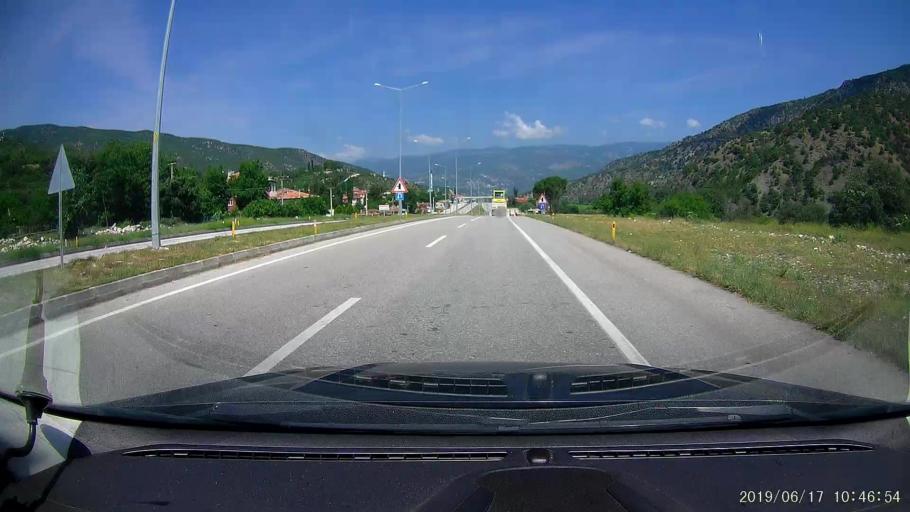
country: TR
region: Corum
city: Hacihamza
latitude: 41.0727
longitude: 34.4556
